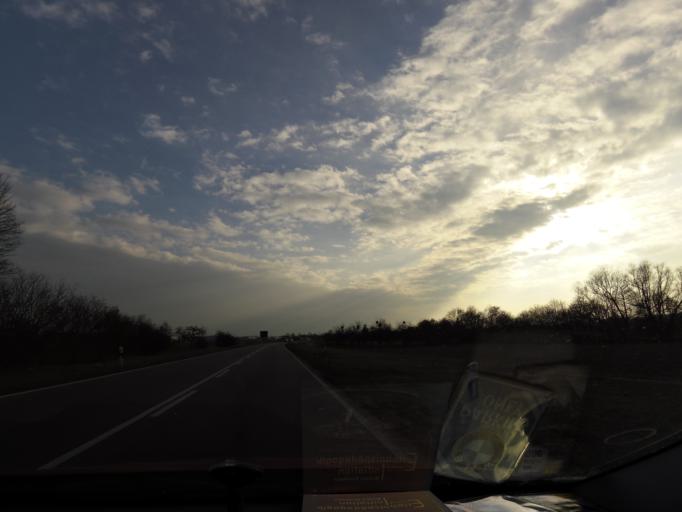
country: DE
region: Baden-Wuerttemberg
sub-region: Freiburg Region
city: Rheinau
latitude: 48.6606
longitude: 7.9365
